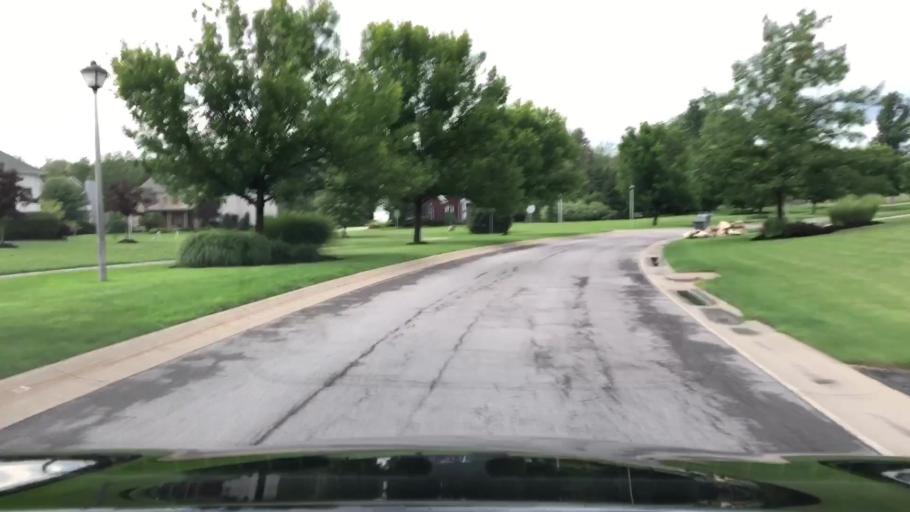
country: US
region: New York
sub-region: Erie County
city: Orchard Park
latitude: 42.7543
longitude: -78.7190
